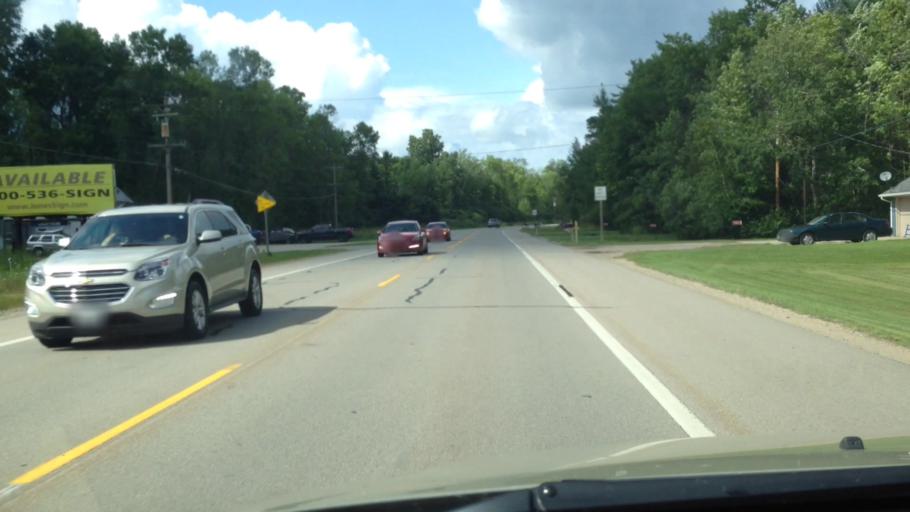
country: US
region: Michigan
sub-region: Menominee County
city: Menominee
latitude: 45.1466
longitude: -87.6030
